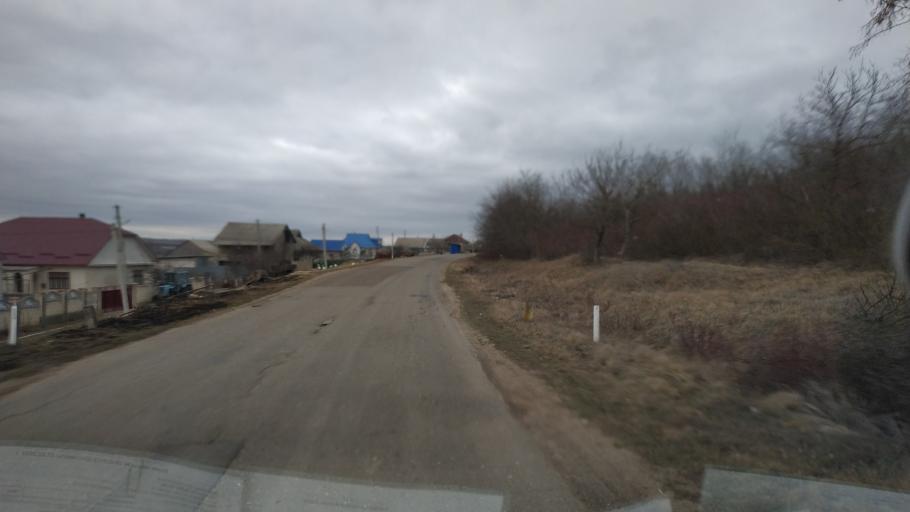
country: MD
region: Causeni
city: Causeni
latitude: 46.6620
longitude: 29.4486
